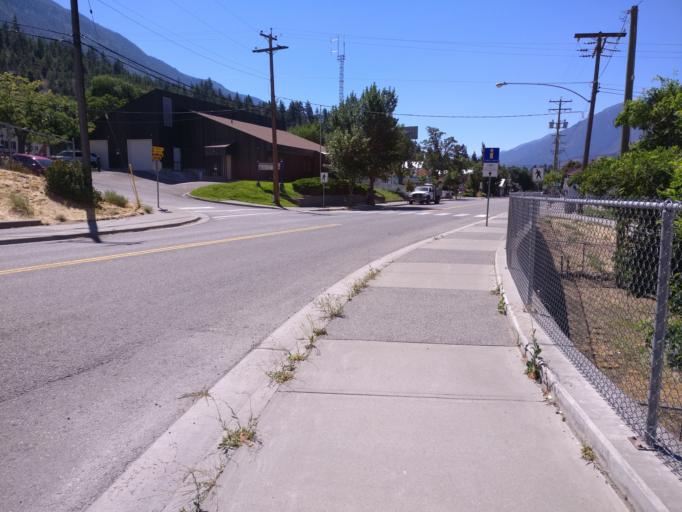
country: CA
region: British Columbia
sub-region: Thompson-Nicola Regional District
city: Ashcroft
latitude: 50.2336
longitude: -121.5808
